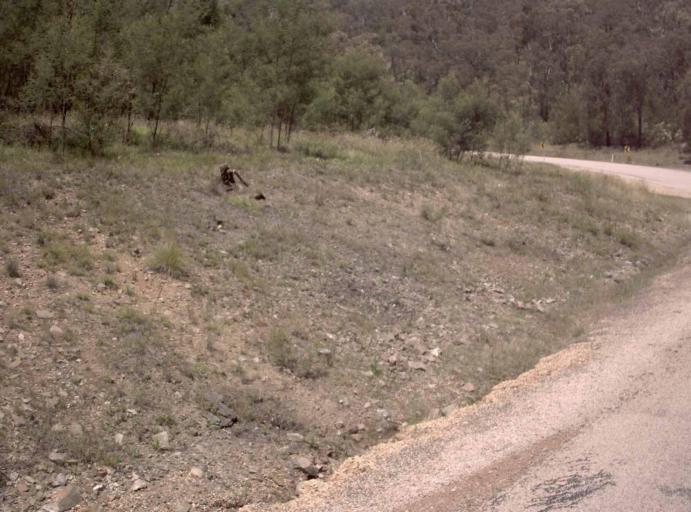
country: AU
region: Victoria
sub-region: East Gippsland
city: Bairnsdale
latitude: -37.4489
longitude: 147.8265
